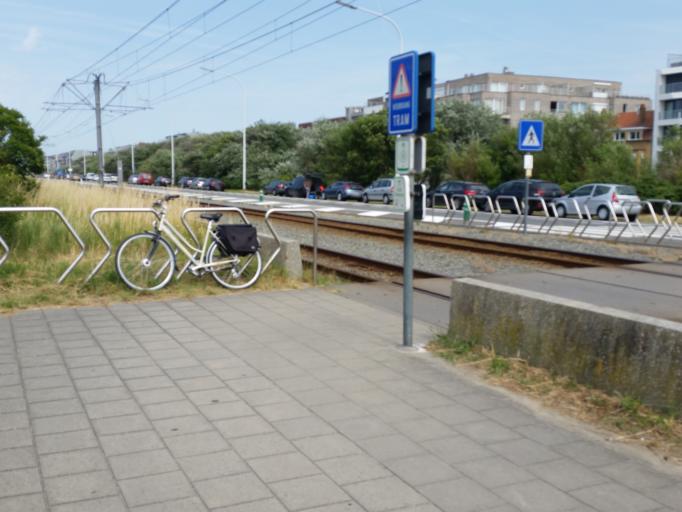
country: BE
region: Flanders
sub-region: Provincie West-Vlaanderen
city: Bredene
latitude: 51.2455
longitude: 2.9531
